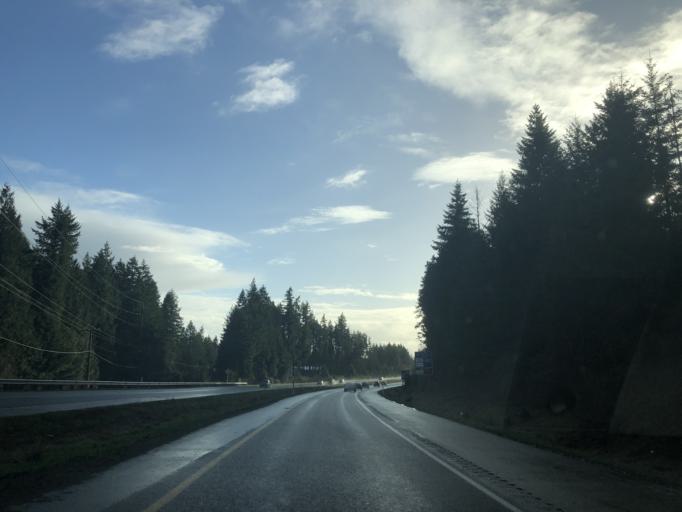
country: US
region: Washington
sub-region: Kitsap County
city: Poulsbo
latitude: 47.7675
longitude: -122.6509
